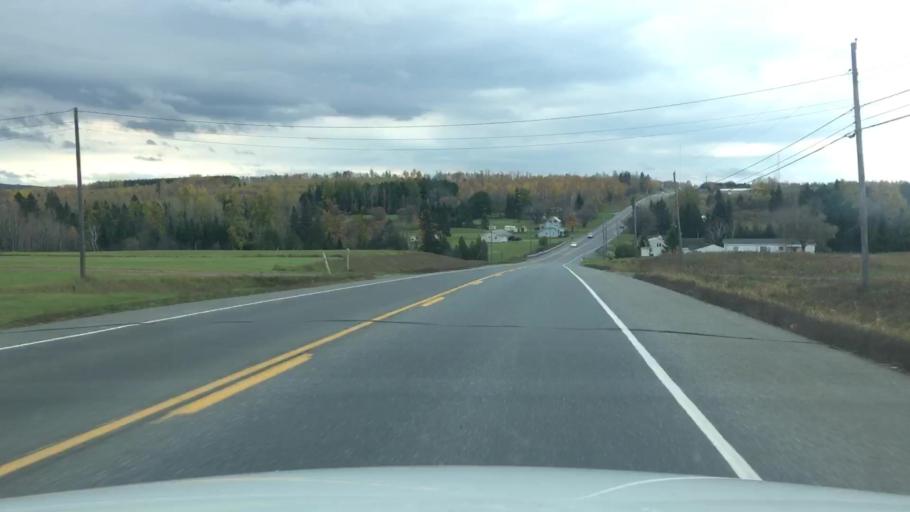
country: US
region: Maine
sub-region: Aroostook County
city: Caribou
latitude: 46.7862
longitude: -67.9894
